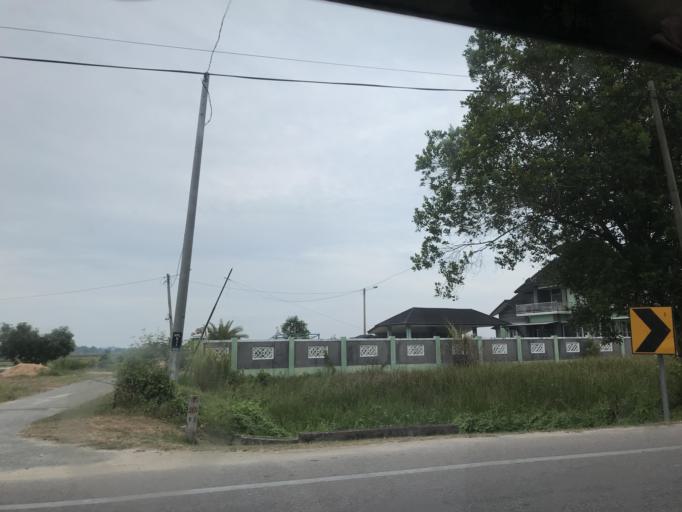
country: MY
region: Kelantan
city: Kota Bharu
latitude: 6.1448
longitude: 102.2185
